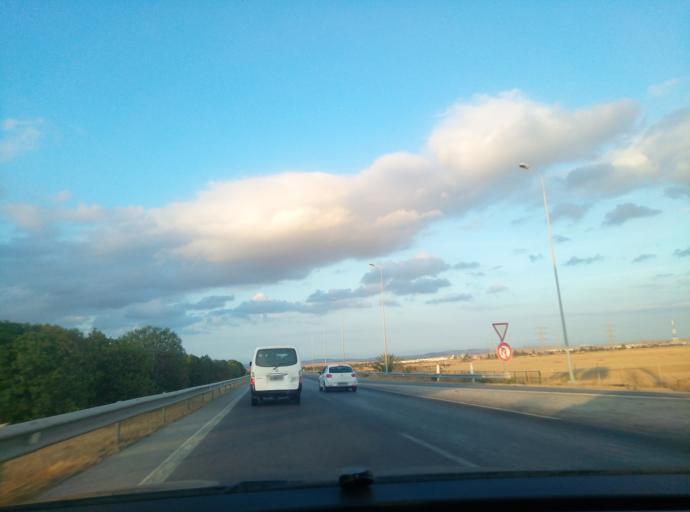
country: TN
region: Manouba
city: El Battan
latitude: 36.6842
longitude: 9.9154
